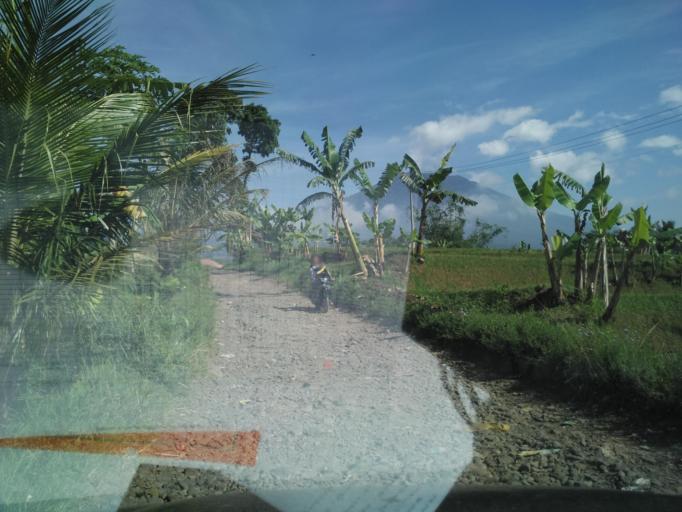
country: ID
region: West Java
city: Cibeber
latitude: -6.8506
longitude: 107.0656
